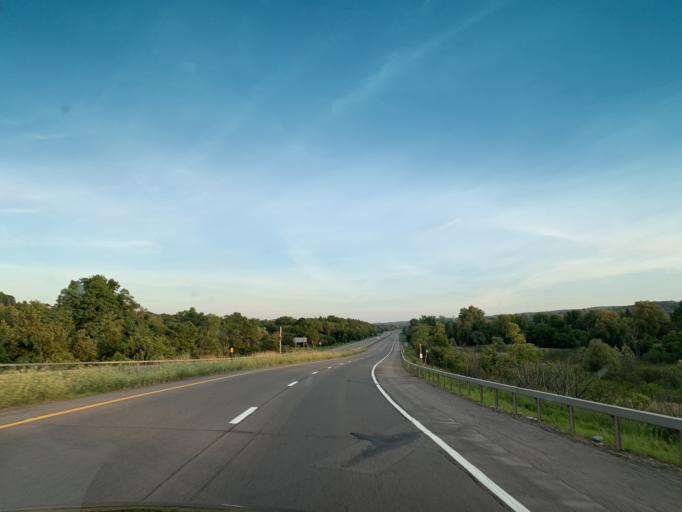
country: US
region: New York
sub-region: Oneida County
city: New Hartford
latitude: 43.0671
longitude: -75.2763
